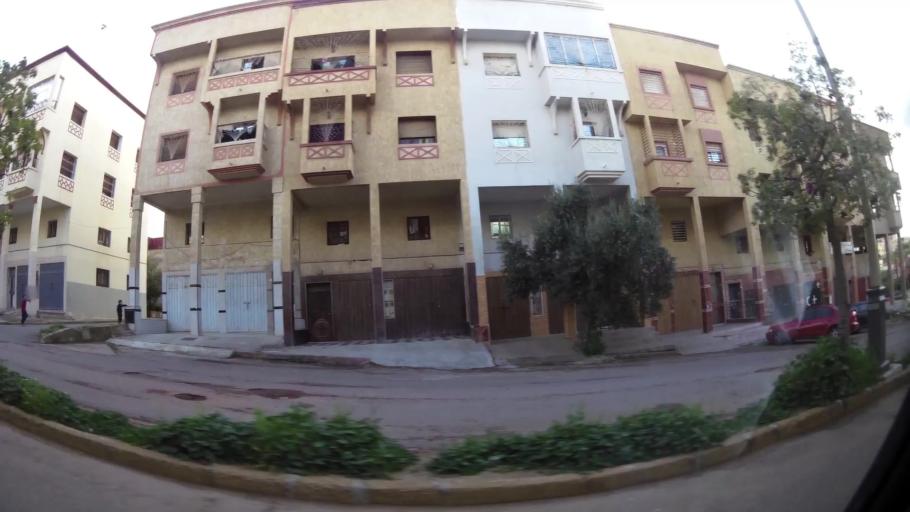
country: MA
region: Chaouia-Ouardigha
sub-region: Settat Province
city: Settat
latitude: 33.0052
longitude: -7.6386
